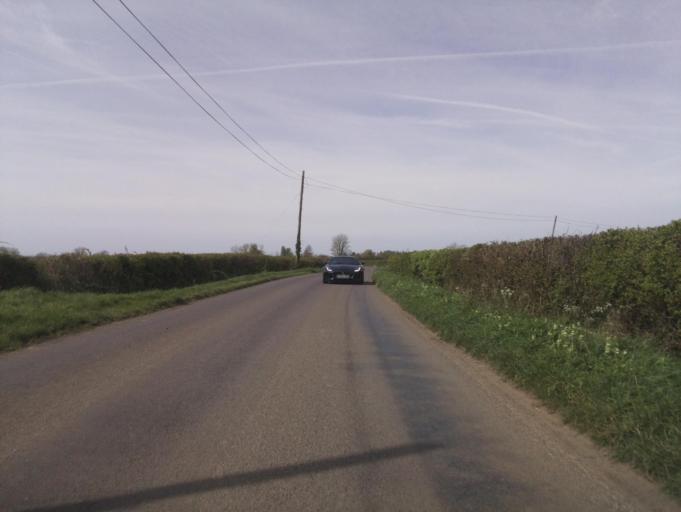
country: GB
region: England
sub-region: Somerset
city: Yeovil
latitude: 51.0167
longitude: -2.5878
